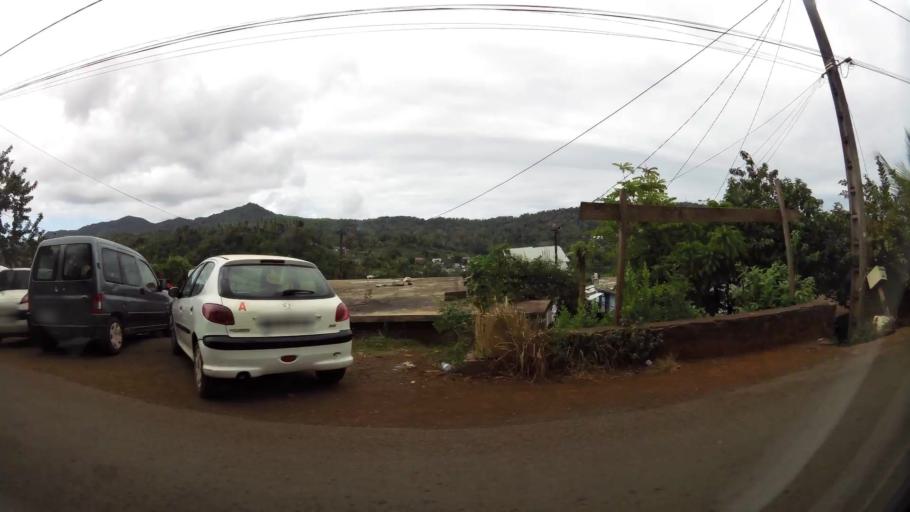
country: YT
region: Chiconi
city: Chiconi
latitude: -12.8378
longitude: 45.1171
